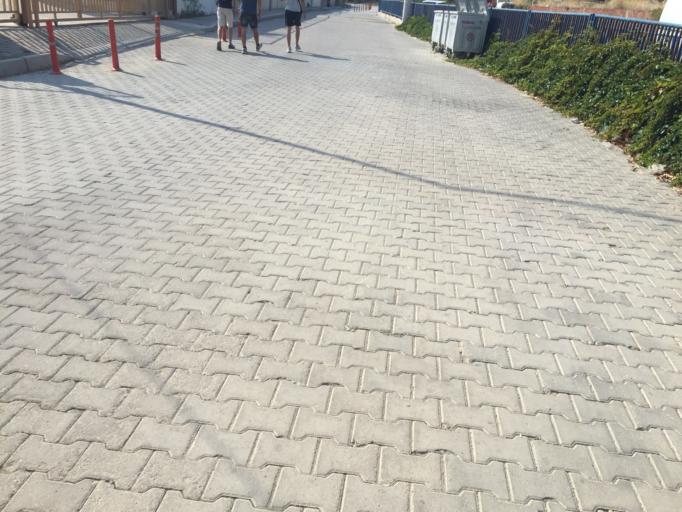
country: TR
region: Izmir
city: Urla
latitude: 38.3254
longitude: 26.7644
